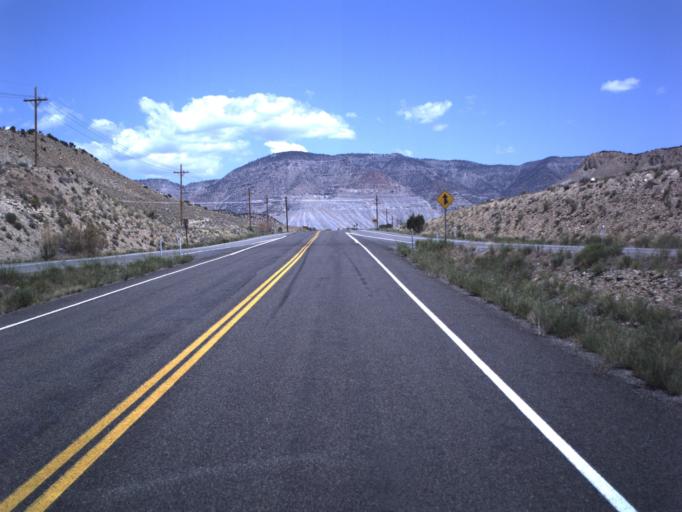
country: US
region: Utah
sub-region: Emery County
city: Orangeville
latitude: 39.2565
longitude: -111.0980
